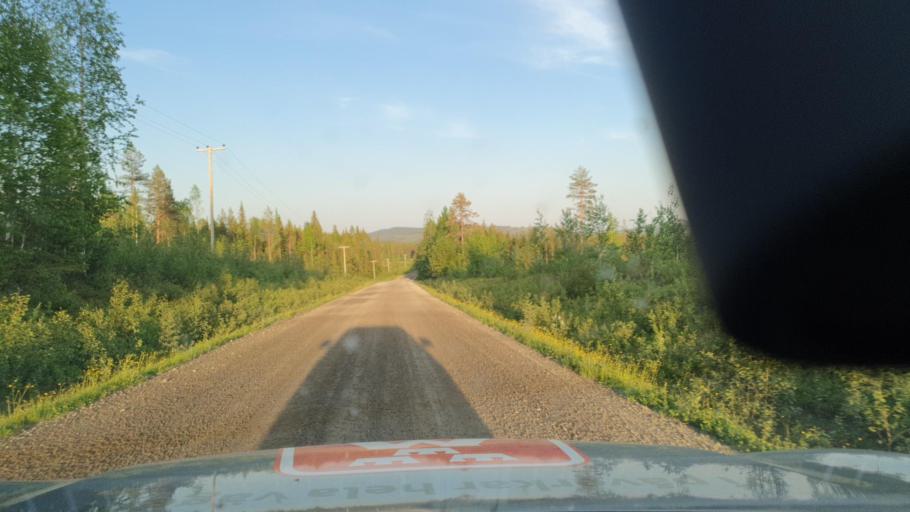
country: SE
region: Norrbotten
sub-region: Bodens Kommun
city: Boden
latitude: 66.1704
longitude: 21.5292
